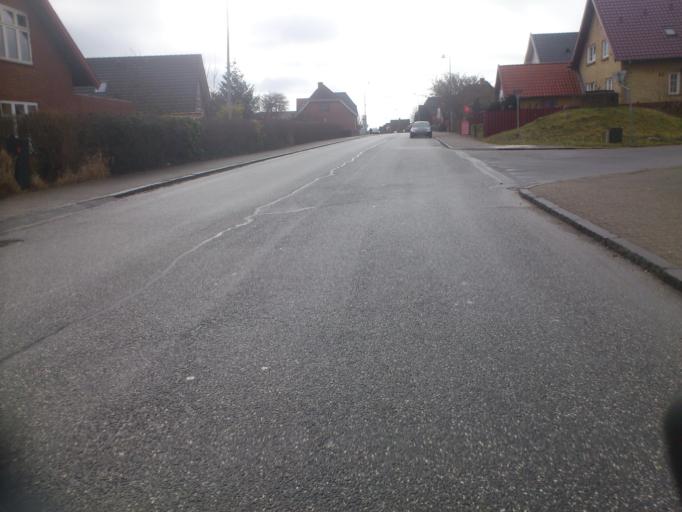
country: DK
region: South Denmark
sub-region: Fredericia Kommune
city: Fredericia
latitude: 55.5768
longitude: 9.7536
